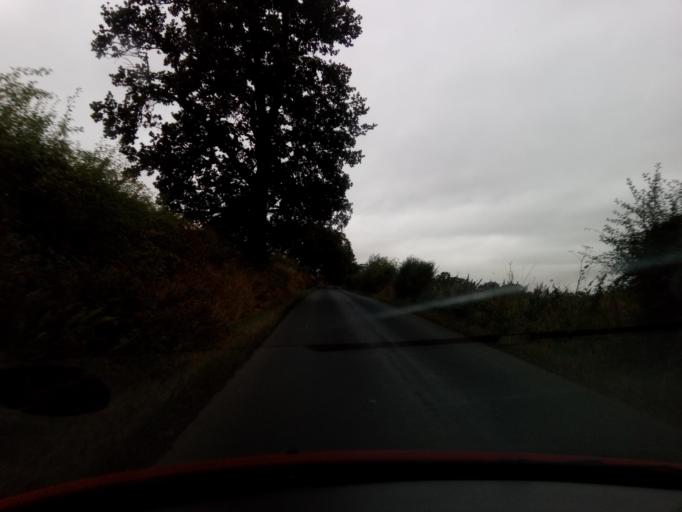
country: GB
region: Scotland
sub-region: The Scottish Borders
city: Saint Boswells
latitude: 55.5166
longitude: -2.6197
